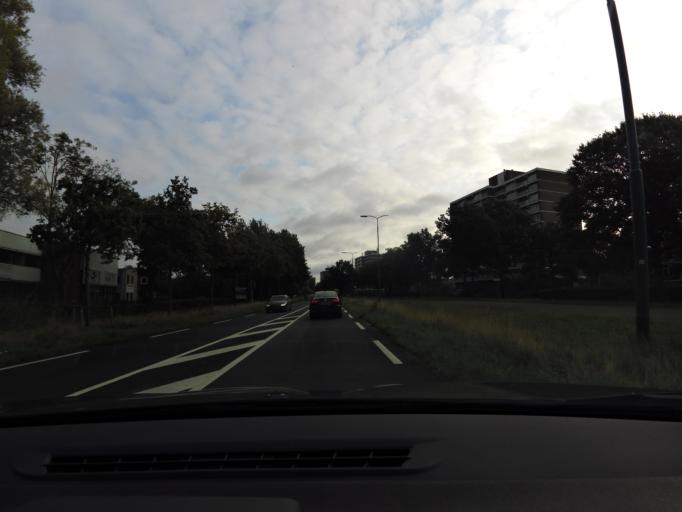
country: NL
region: Utrecht
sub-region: Gemeente De Bilt
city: De Bilt
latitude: 52.1095
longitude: 5.1710
